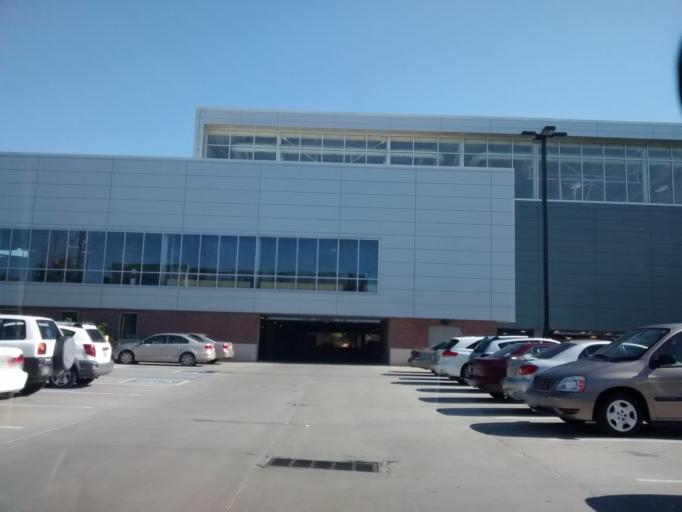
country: US
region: Nebraska
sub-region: Douglas County
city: Ralston
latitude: 41.2573
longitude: -96.0100
